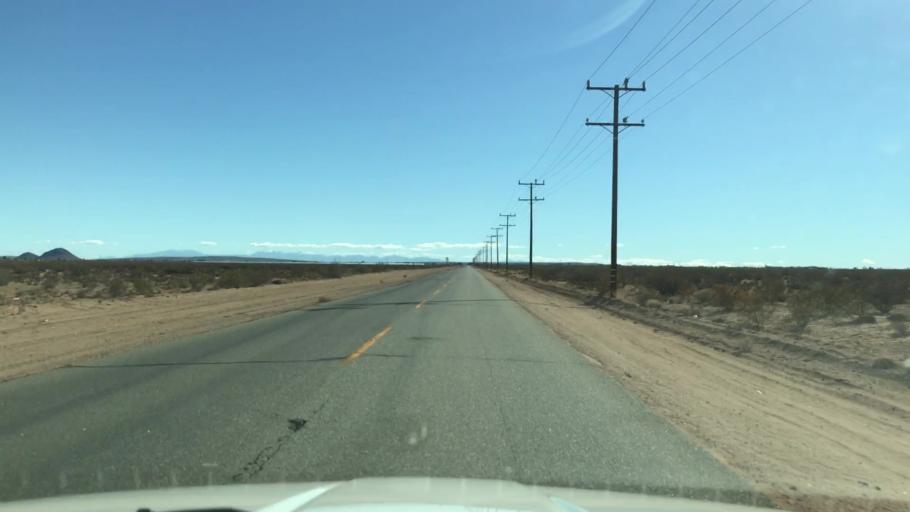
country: US
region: California
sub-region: Kern County
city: California City
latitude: 35.1693
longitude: -117.9858
